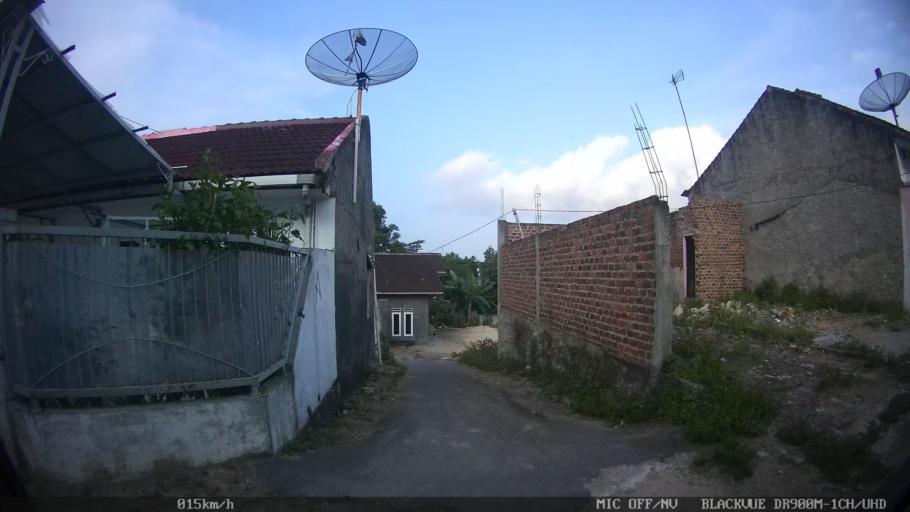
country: ID
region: Lampung
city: Kedaton
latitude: -5.4009
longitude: 105.2944
